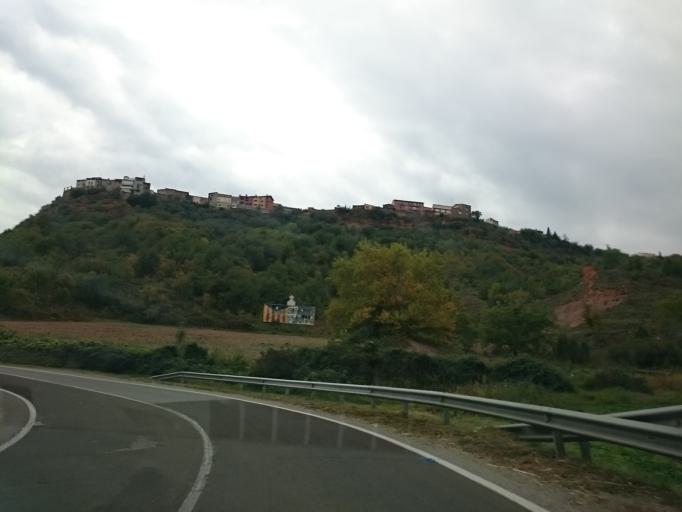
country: ES
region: Catalonia
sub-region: Provincia de Lleida
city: Tremp
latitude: 42.1886
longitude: 0.9036
